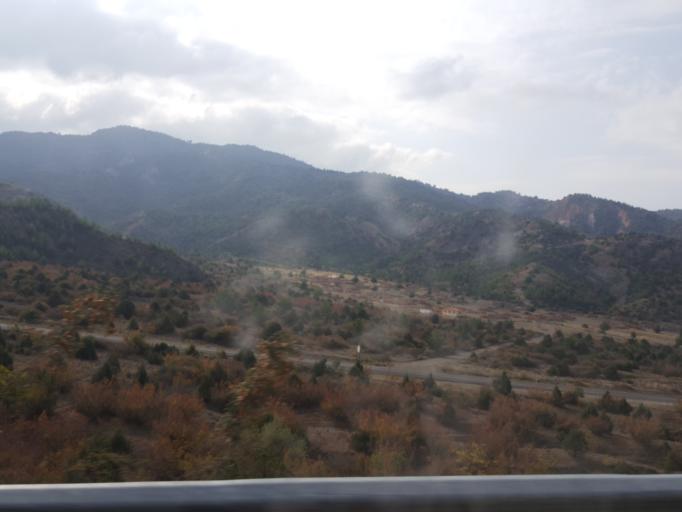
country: TR
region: Corum
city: Kamil
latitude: 41.1071
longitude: 34.7408
